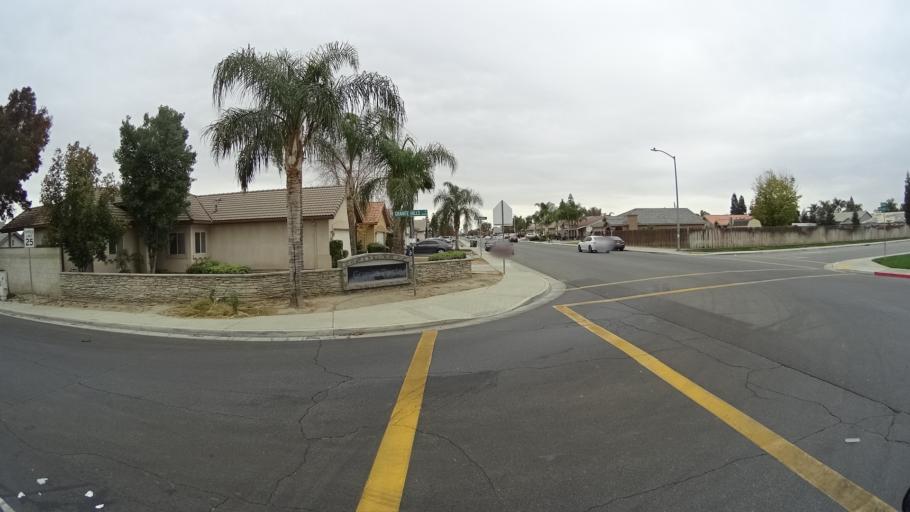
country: US
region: California
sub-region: Kern County
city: Greenfield
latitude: 35.2886
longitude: -119.0352
